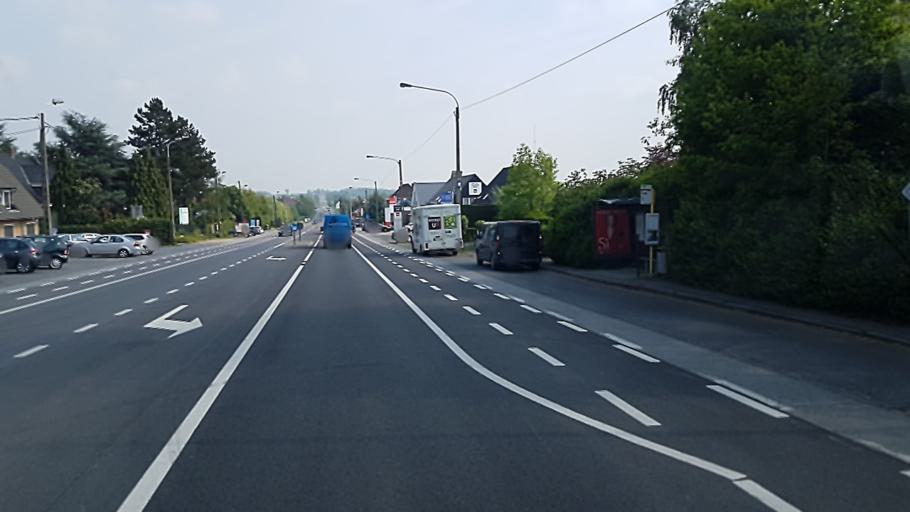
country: BE
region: Flanders
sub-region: Provincie West-Vlaanderen
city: Kortrijk
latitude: 50.7978
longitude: 3.2864
